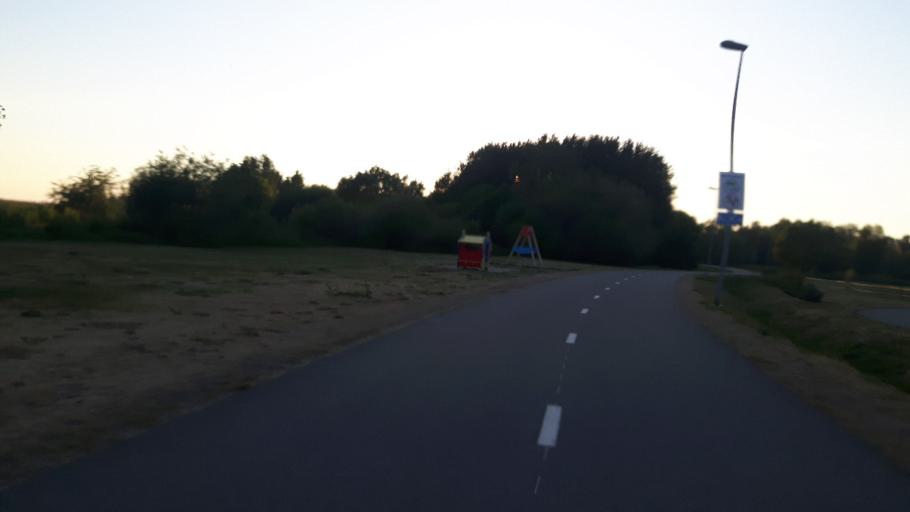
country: EE
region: Paernumaa
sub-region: Paernu linn
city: Parnu
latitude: 58.3688
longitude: 24.5332
